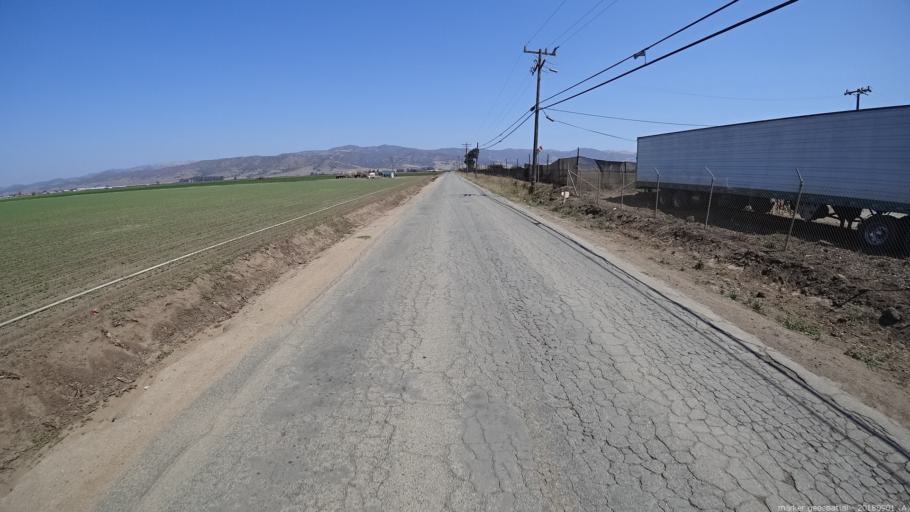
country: US
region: California
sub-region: Monterey County
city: Chualar
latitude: 36.6146
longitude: -121.5438
